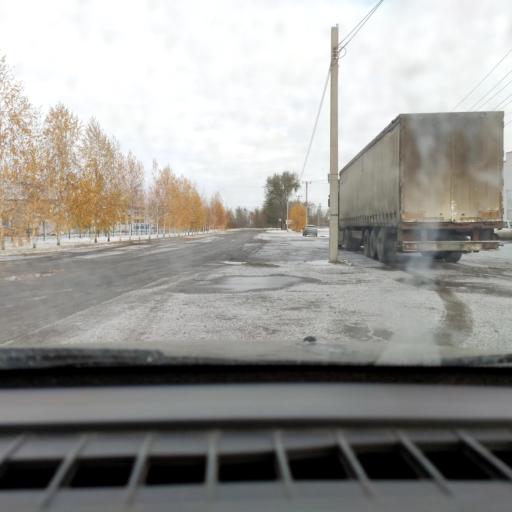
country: RU
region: Samara
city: Tol'yatti
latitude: 53.5776
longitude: 49.2844
